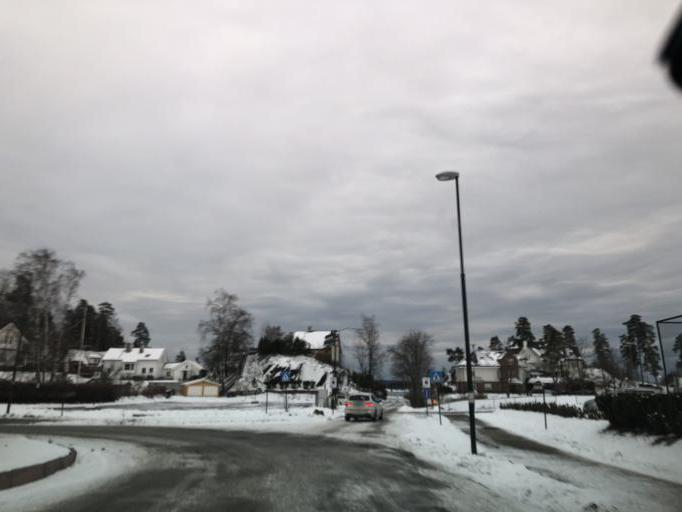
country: NO
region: Akershus
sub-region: Baerum
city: Sandvika
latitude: 59.8596
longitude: 10.5171
